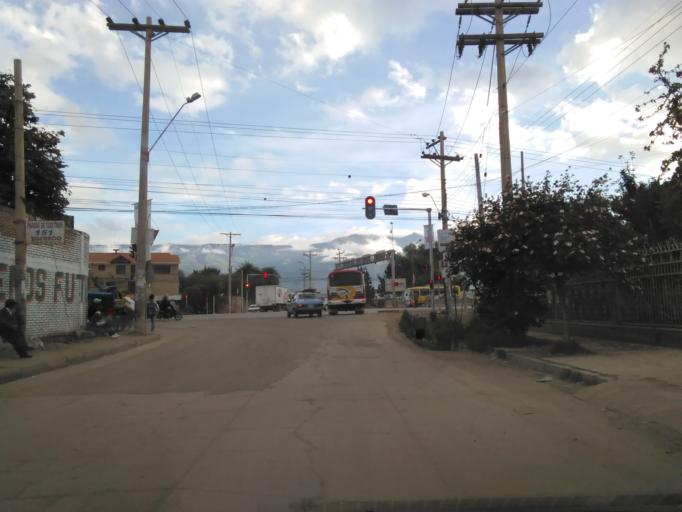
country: BO
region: Cochabamba
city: Cochabamba
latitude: -17.3918
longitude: -66.2301
